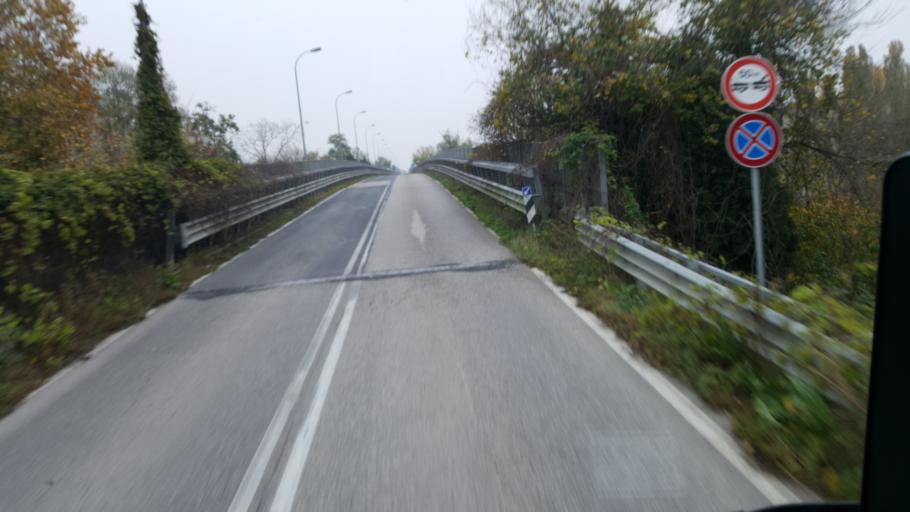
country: IT
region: Veneto
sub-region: Provincia di Rovigo
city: Ficarolo
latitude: 44.9456
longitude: 11.4211
